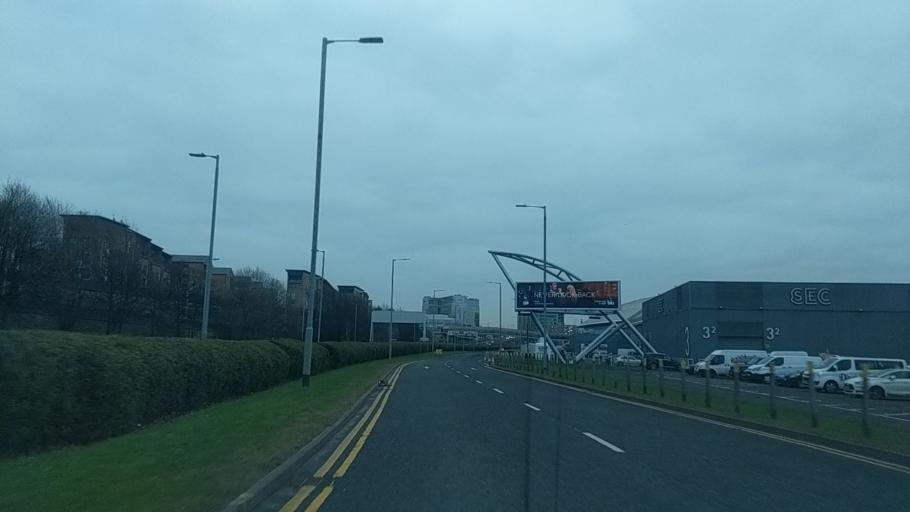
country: GB
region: Scotland
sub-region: Glasgow City
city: Glasgow
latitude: 55.8627
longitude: -4.2926
